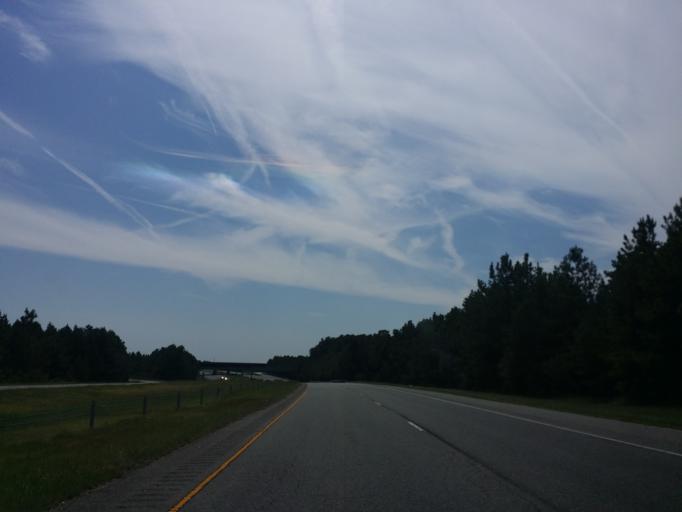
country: US
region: North Carolina
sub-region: Wake County
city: Morrisville
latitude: 35.8990
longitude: -78.8130
